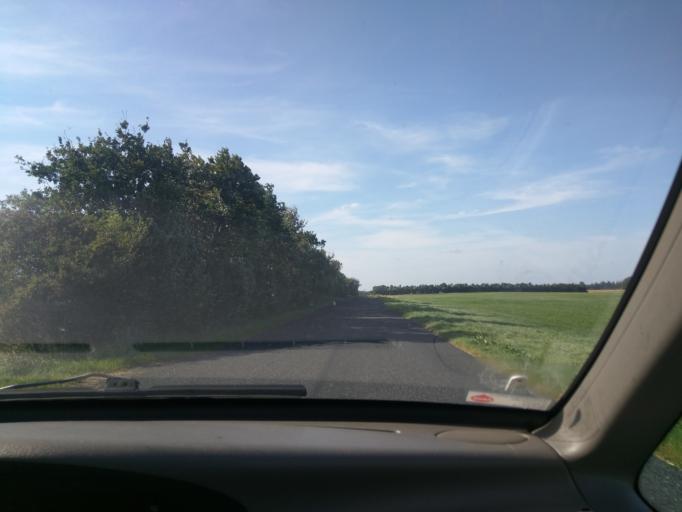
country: DK
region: Central Jutland
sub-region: Viborg Kommune
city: Bjerringbro
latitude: 56.4876
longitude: 9.5958
